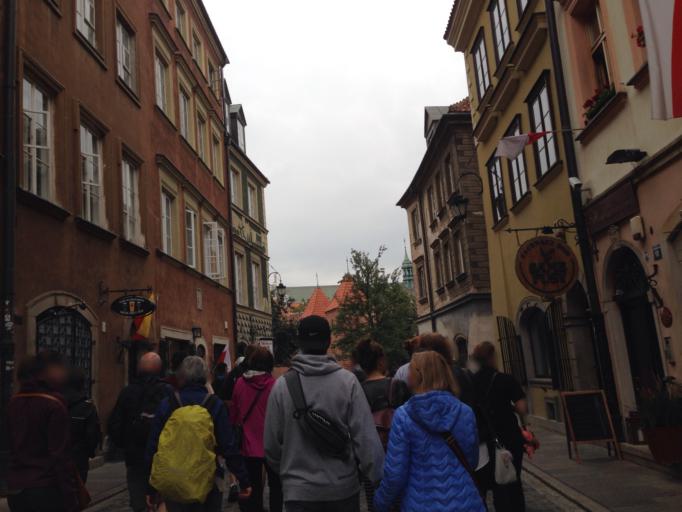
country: PL
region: Masovian Voivodeship
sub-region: Warszawa
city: Warsaw
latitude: 52.2499
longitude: 21.0108
